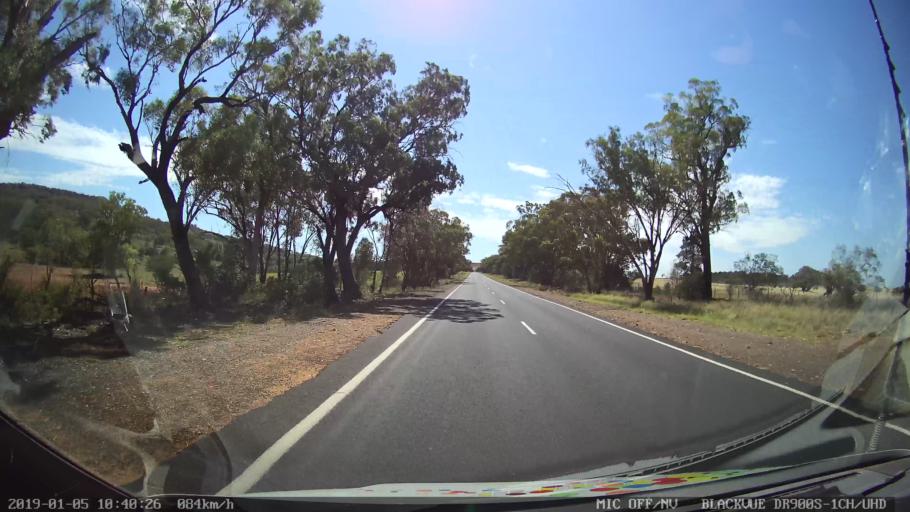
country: AU
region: New South Wales
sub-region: Gilgandra
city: Gilgandra
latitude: -31.4658
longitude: 148.9443
